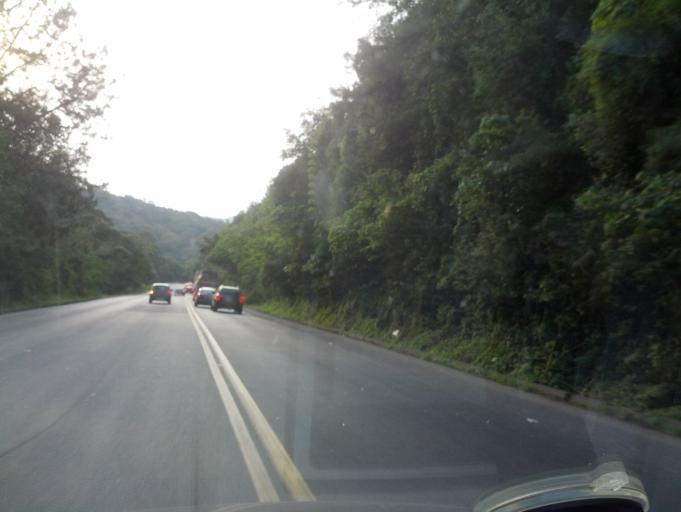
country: BR
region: Santa Catarina
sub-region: Otacilio Costa
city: Otacilio Costa
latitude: -27.2956
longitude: -50.0763
